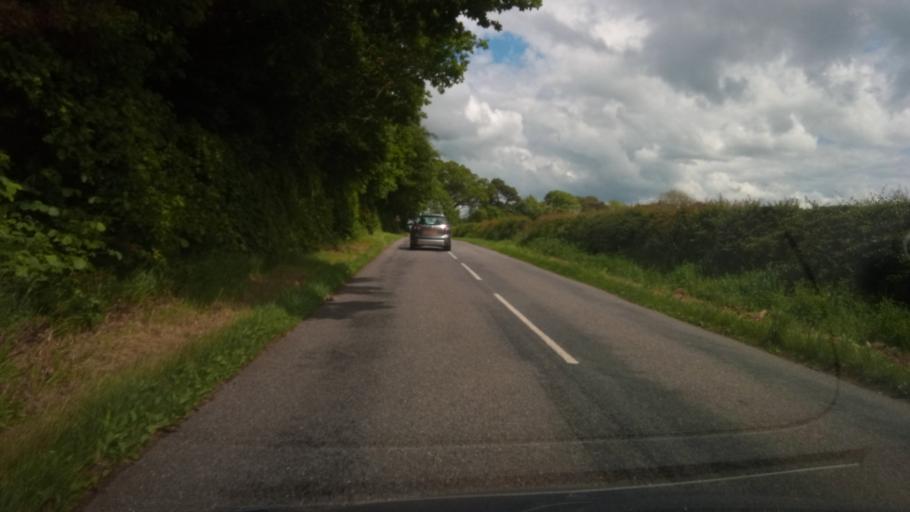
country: GB
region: Scotland
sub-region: The Scottish Borders
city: Kelso
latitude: 55.5852
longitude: -2.3823
